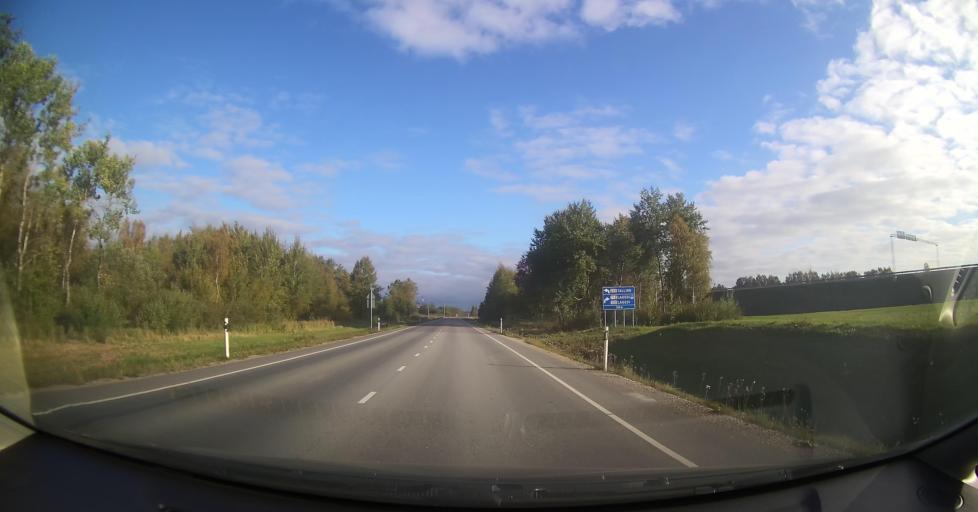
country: EE
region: Harju
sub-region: Joelaehtme vald
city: Loo
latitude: 59.4044
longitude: 24.9128
